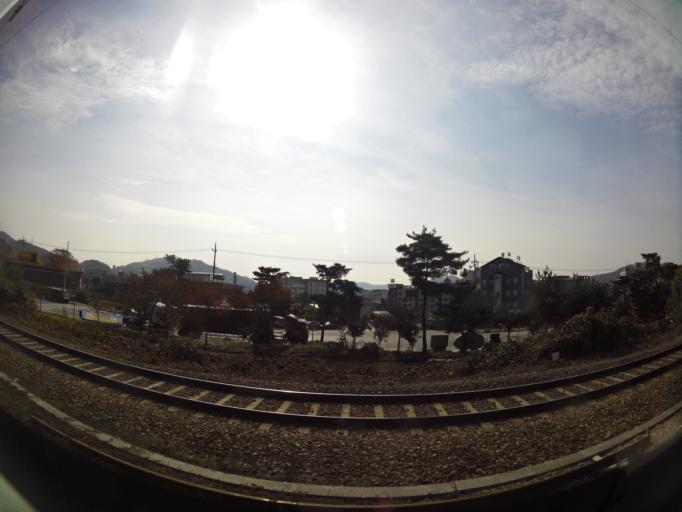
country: KR
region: Daejeon
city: Sintansin
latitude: 36.5317
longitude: 127.3688
